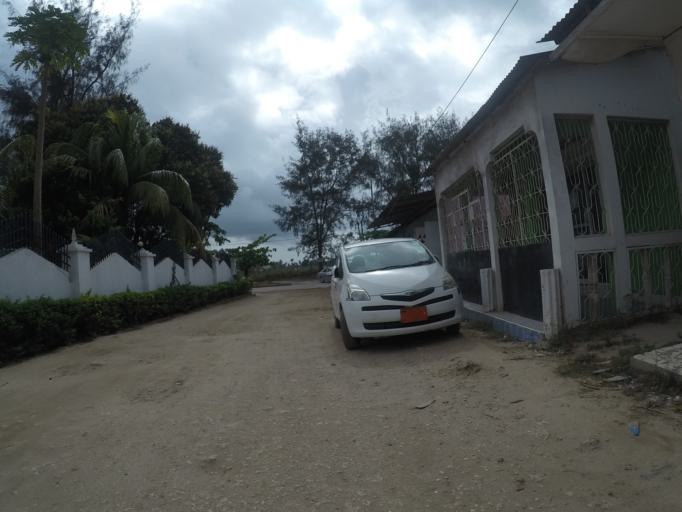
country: TZ
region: Zanzibar Urban/West
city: Zanzibar
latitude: -6.2153
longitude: 39.2188
